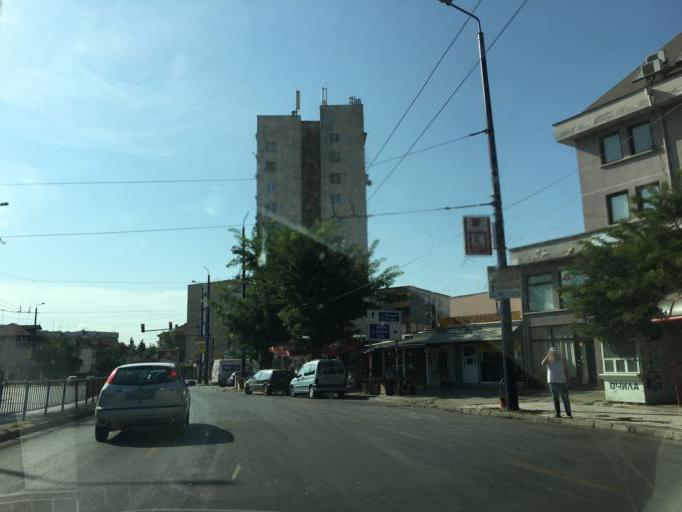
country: BG
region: Pazardzhik
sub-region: Obshtina Pazardzhik
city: Pazardzhik
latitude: 42.1965
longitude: 24.3337
